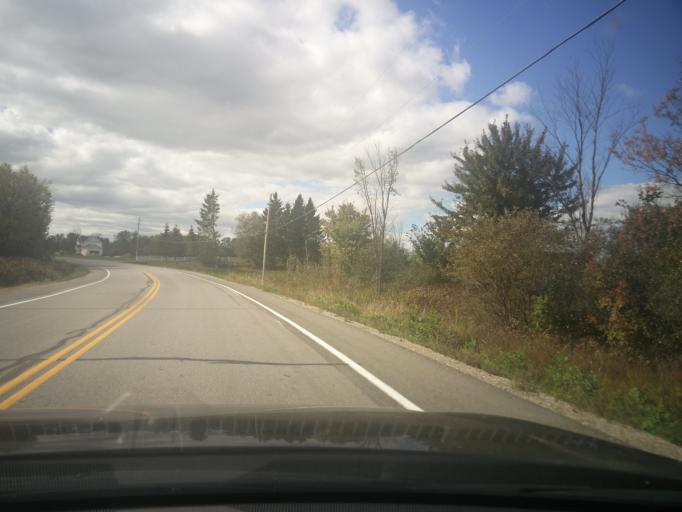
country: CA
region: Ontario
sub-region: Lanark County
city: Smiths Falls
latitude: 44.9788
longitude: -76.1300
